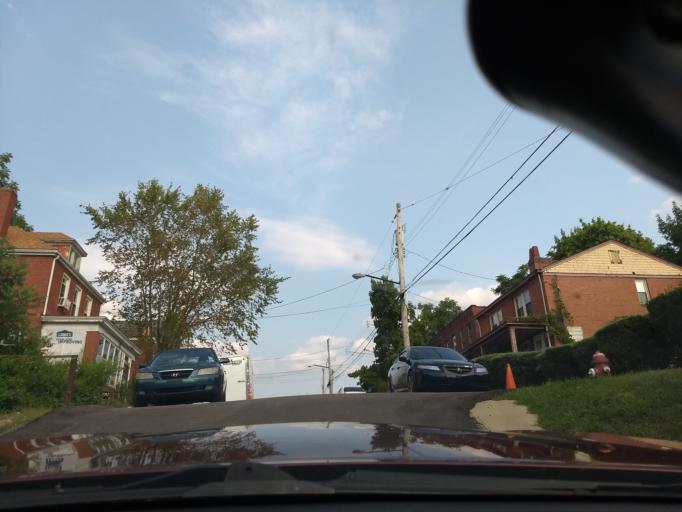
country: US
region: Pennsylvania
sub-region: Allegheny County
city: Wilkinsburg
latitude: 40.4628
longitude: -79.9005
